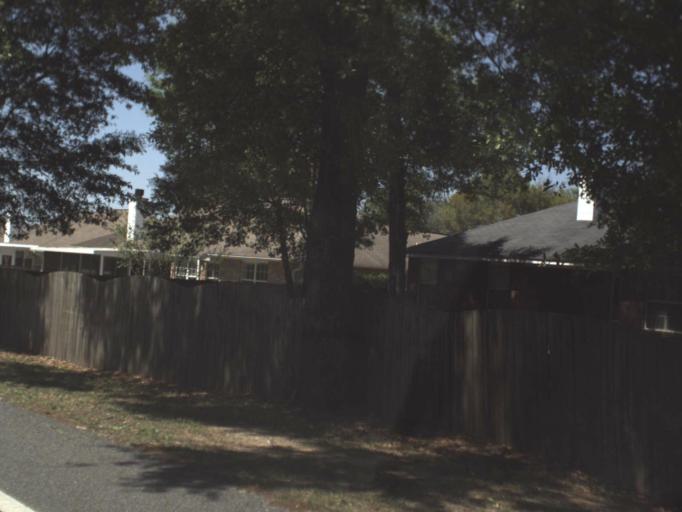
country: US
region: Florida
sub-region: Escambia County
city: Bellview
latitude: 30.4878
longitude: -87.3171
